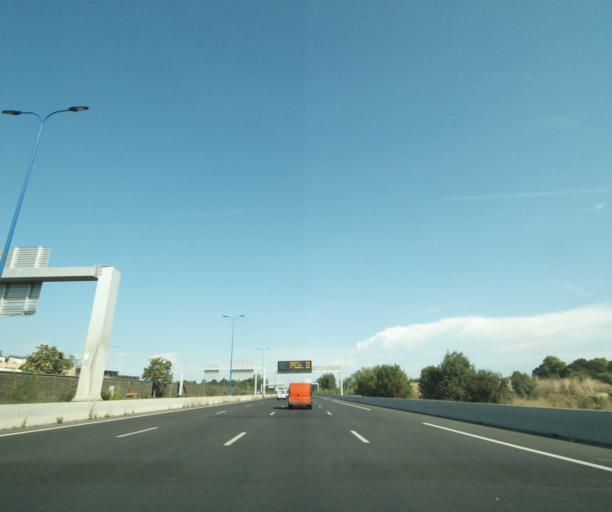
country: FR
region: Midi-Pyrenees
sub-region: Departement de la Haute-Garonne
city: Ramonville-Saint-Agne
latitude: 43.5639
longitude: 1.4866
